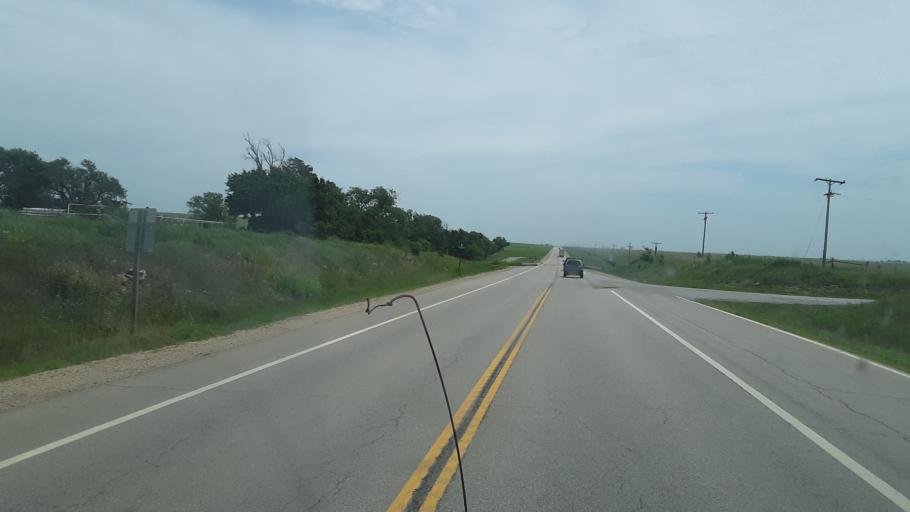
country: US
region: Kansas
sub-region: Greenwood County
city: Eureka
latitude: 37.8102
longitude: -96.4500
